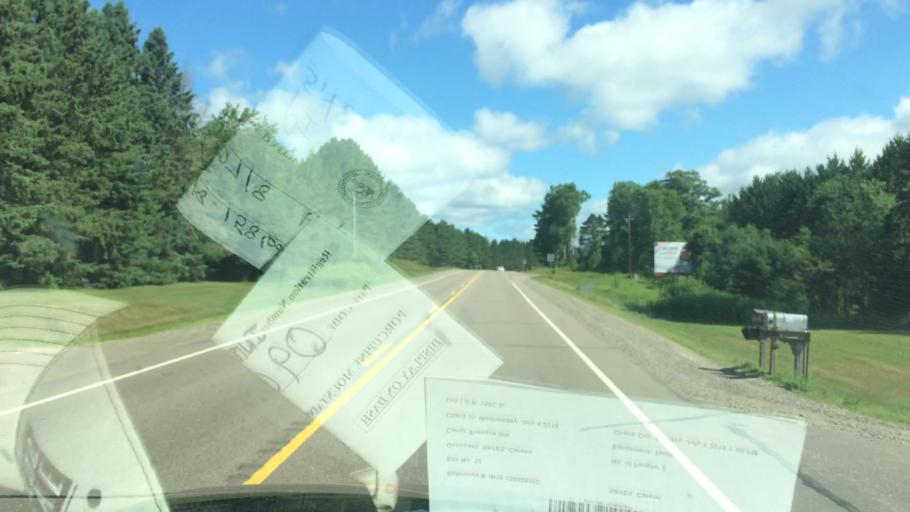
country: US
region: Wisconsin
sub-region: Oneida County
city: Rhinelander
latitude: 45.5872
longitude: -89.5694
